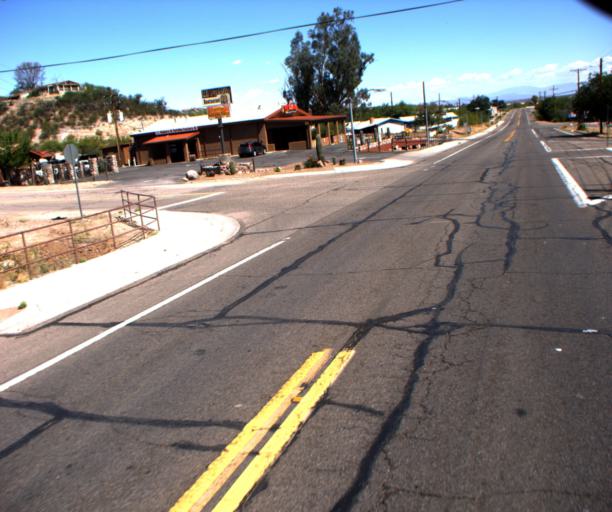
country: US
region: Arizona
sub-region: Pinal County
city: Mammoth
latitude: 32.7302
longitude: -110.6471
